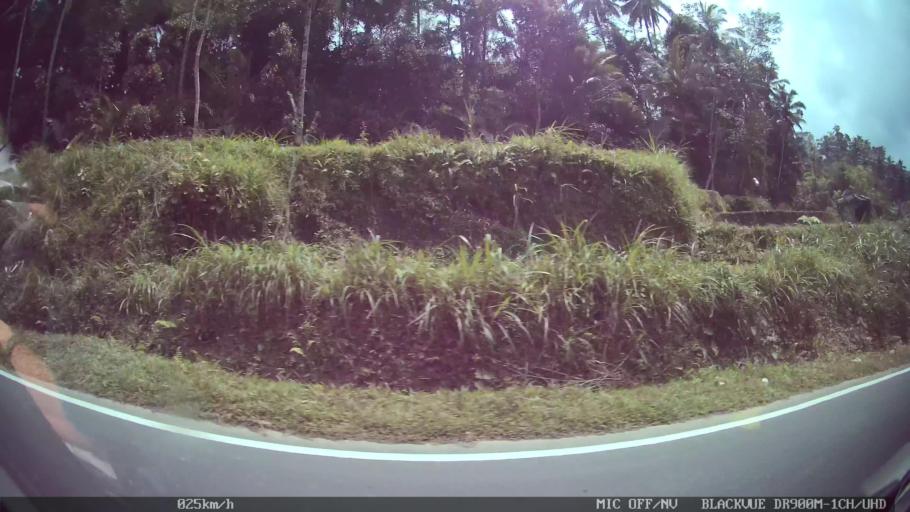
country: ID
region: Bali
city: Banjar Geriana Kangin
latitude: -8.4208
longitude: 115.4377
